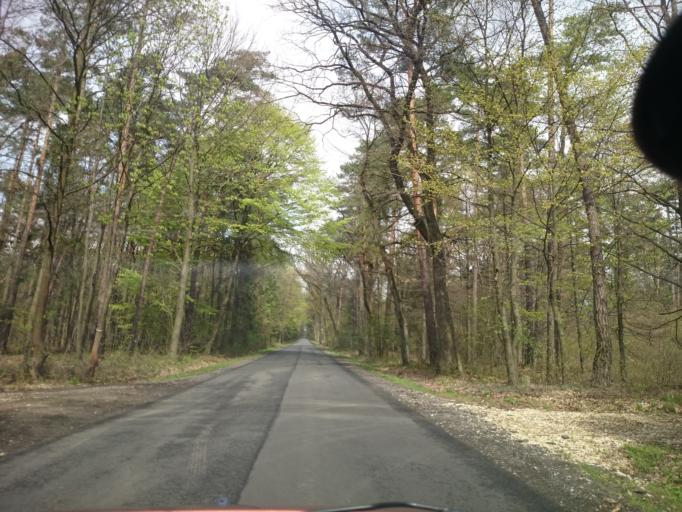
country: PL
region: Opole Voivodeship
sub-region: Powiat strzelecki
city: Izbicko
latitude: 50.5408
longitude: 18.1372
